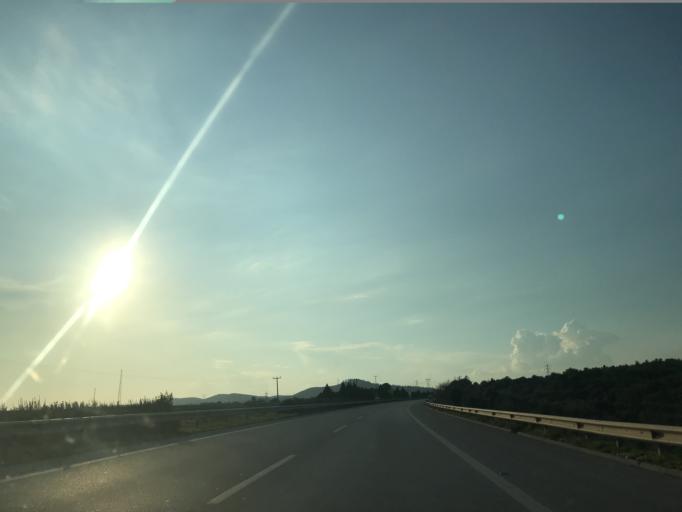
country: TR
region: Osmaniye
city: Toprakkale
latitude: 36.9670
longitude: 36.0422
